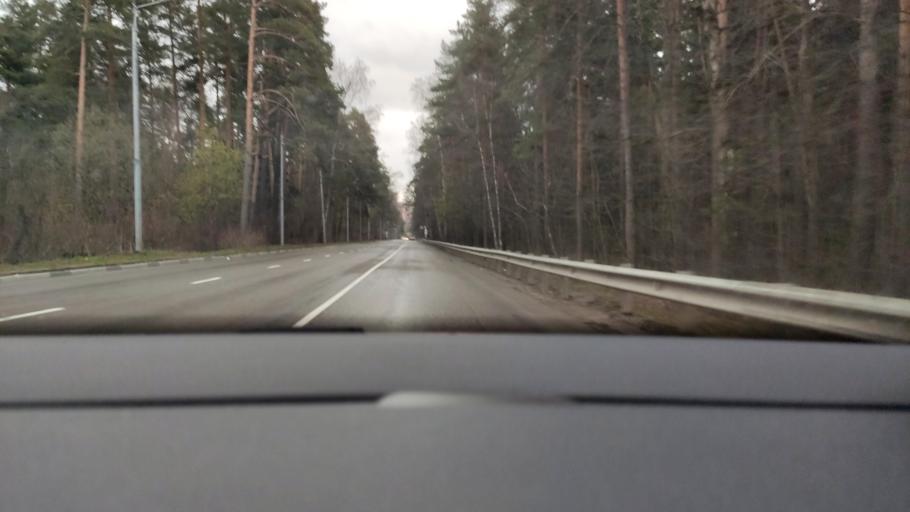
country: RU
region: Moscow
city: Vostochnyy
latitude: 55.8266
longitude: 37.9040
